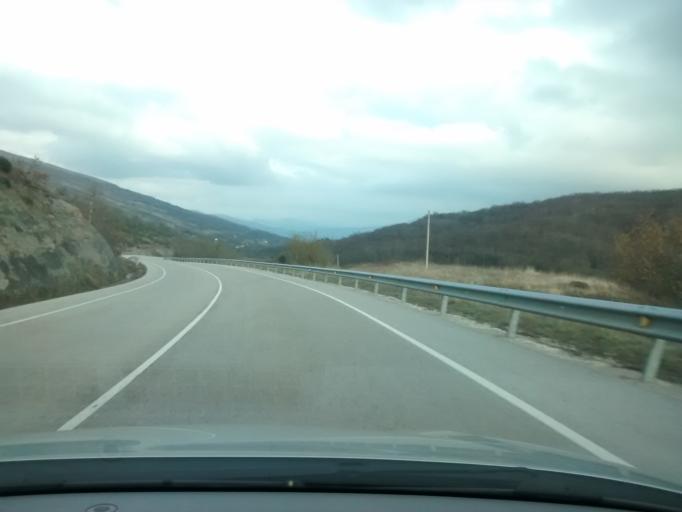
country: ES
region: Castille and Leon
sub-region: Provincia de Burgos
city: Espinosa de los Monteros
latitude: 43.0924
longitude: -3.4313
